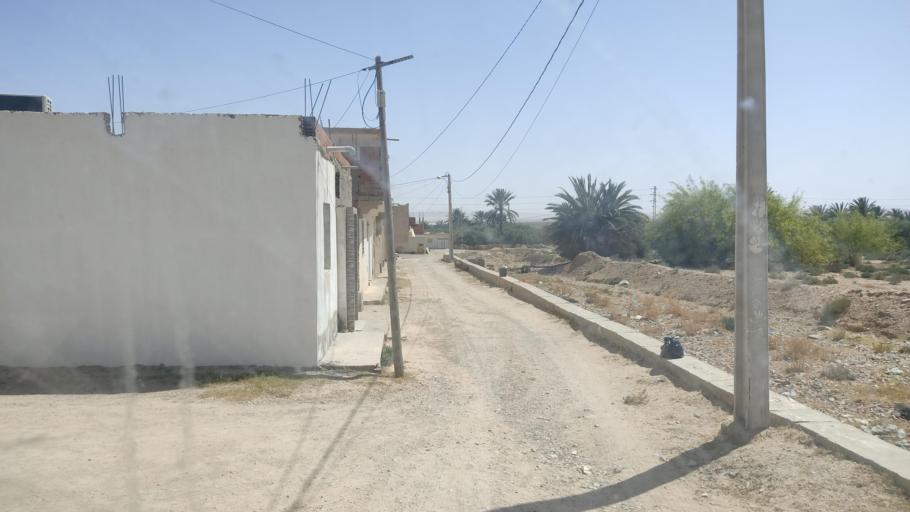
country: TN
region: Gafsa
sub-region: Gafsa Municipality
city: Gafsa
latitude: 34.3382
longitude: 8.9202
